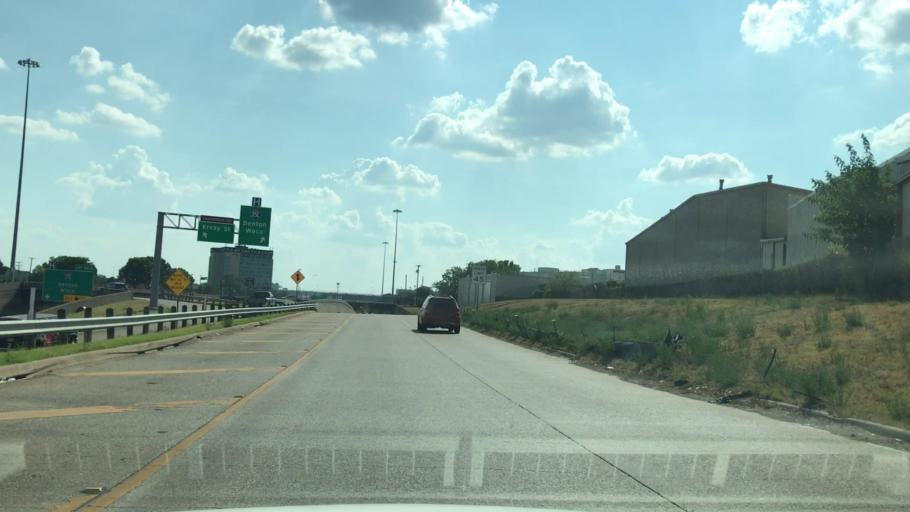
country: US
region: Texas
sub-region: Dallas County
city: Dallas
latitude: 32.7756
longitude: -96.7891
